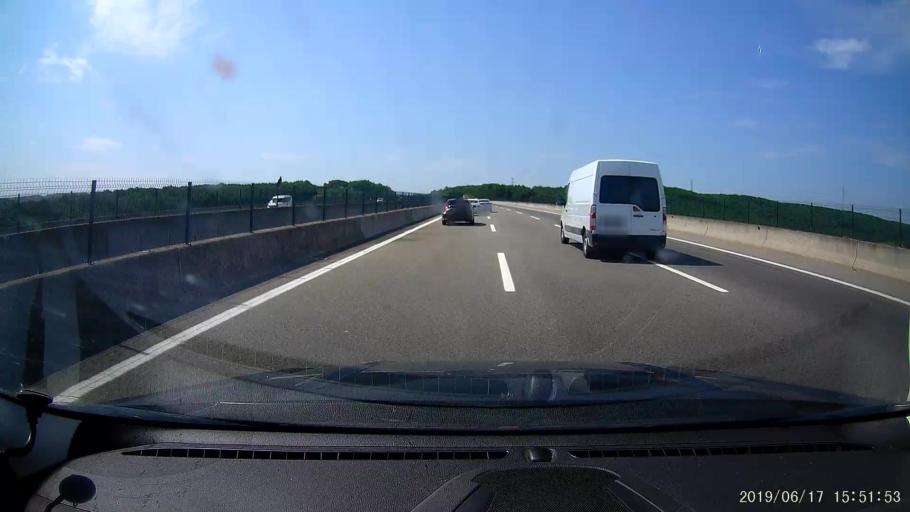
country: TR
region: Istanbul
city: Canta
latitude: 41.1805
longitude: 28.1132
